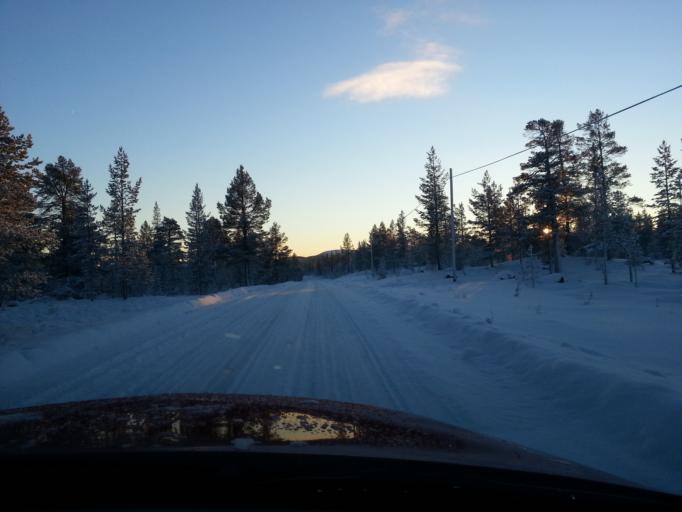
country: SE
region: Jaemtland
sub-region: Harjedalens Kommun
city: Sveg
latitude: 62.2688
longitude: 13.3899
